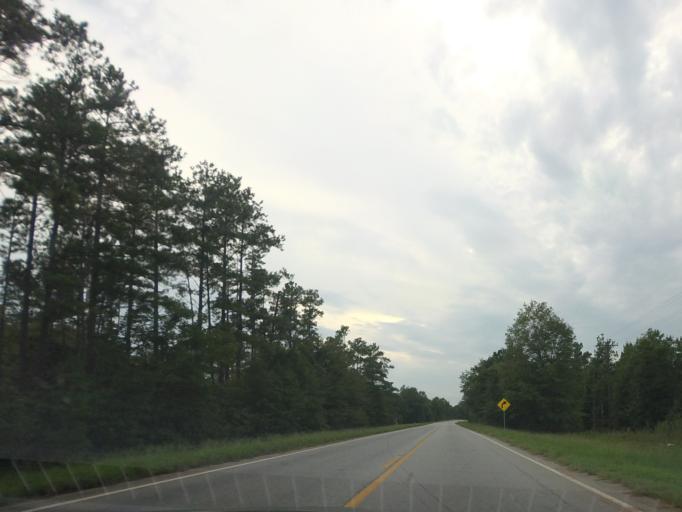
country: US
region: Georgia
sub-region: Twiggs County
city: Jeffersonville
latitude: 32.7615
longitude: -83.4542
